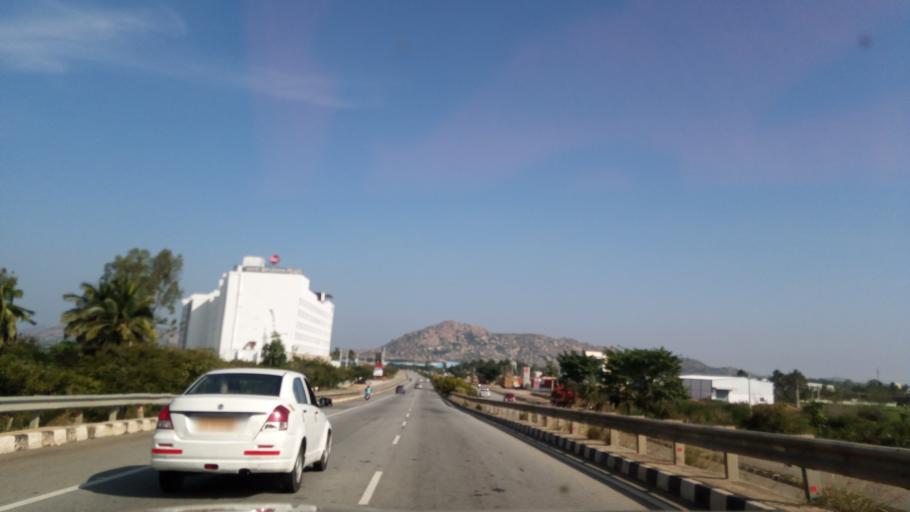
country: IN
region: Karnataka
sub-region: Kolar
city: Malur
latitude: 13.1310
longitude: 77.9867
